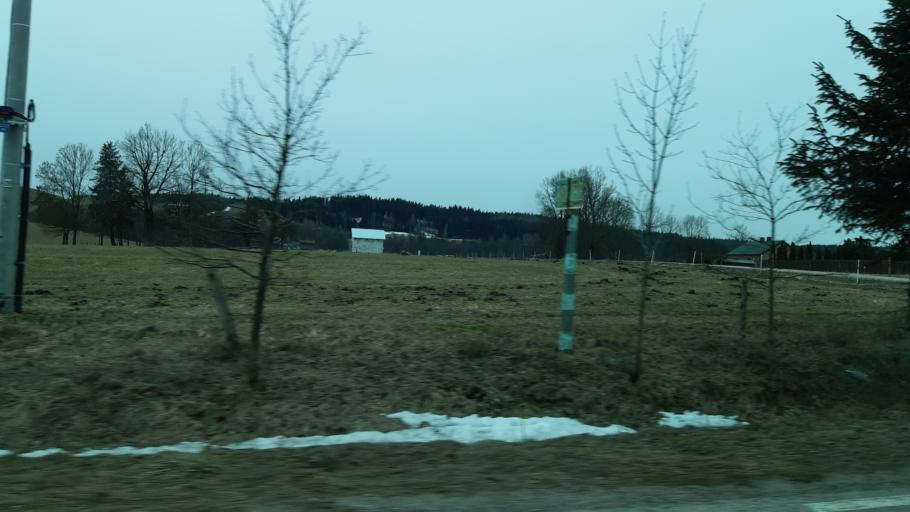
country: PL
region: Podlasie
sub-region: Suwalki
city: Suwalki
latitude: 54.3356
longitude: 22.9279
